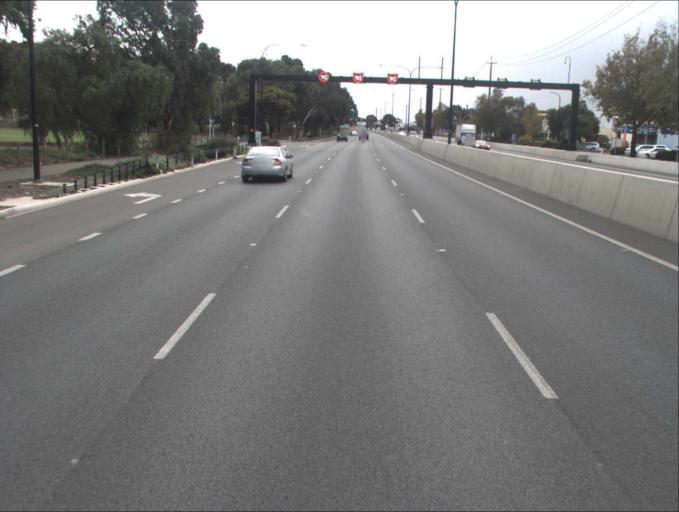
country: AU
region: South Australia
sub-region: Charles Sturt
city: Woodville
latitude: -34.8703
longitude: 138.5708
